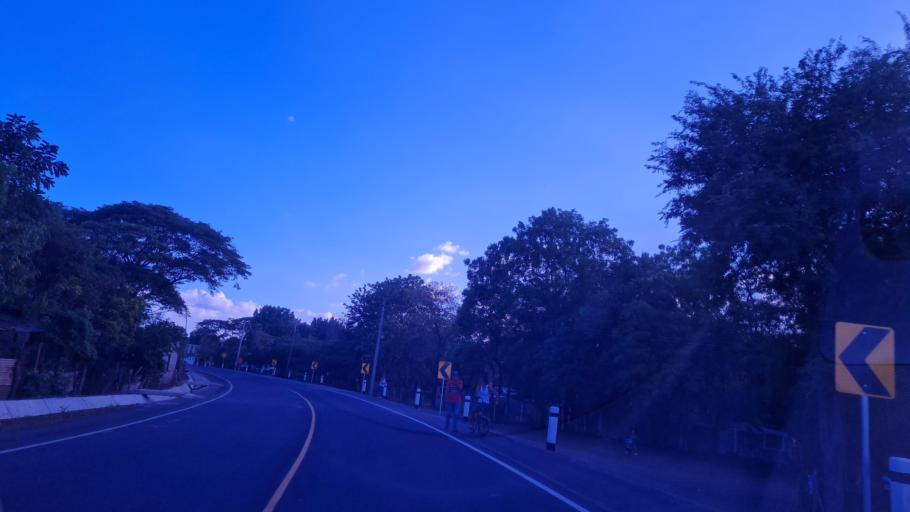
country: NI
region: Masaya
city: Ticuantepe
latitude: 12.0910
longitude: -86.1643
